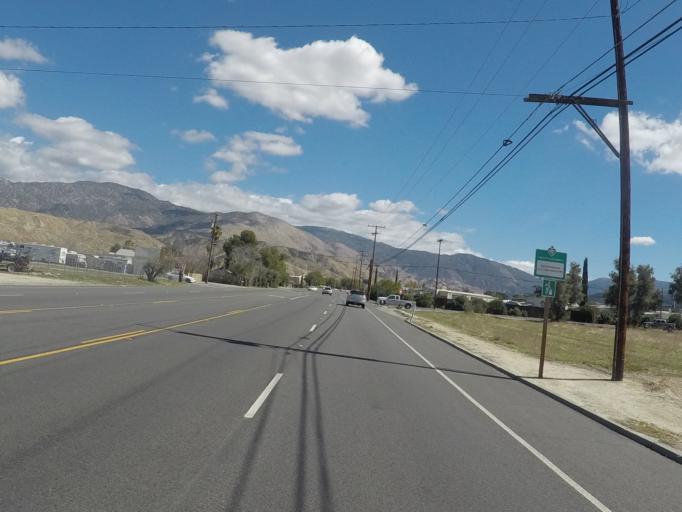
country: US
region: California
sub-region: Riverside County
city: Valle Vista
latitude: 33.7478
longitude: -116.8768
